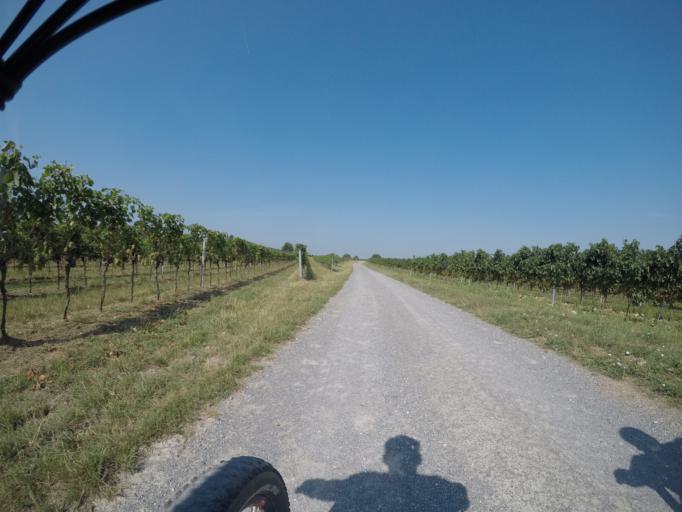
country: AT
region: Lower Austria
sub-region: Politischer Bezirk Baden
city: Hirtenberg
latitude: 47.9512
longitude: 16.1772
